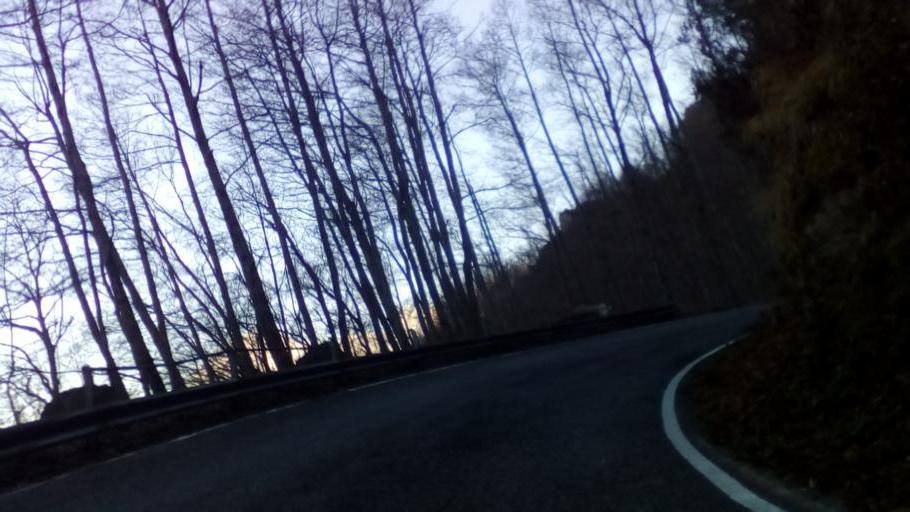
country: IT
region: Tuscany
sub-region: Provincia di Massa-Carrara
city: Montignoso
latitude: 44.0590
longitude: 10.2173
